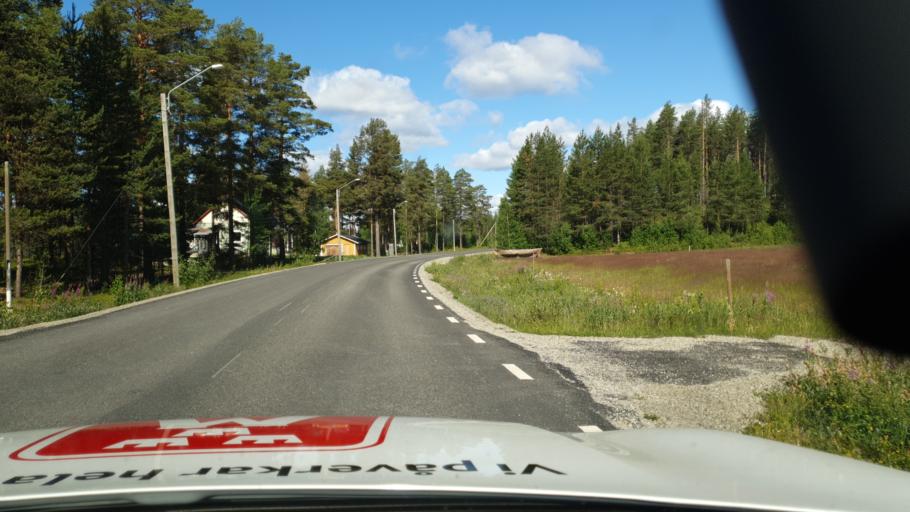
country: SE
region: Vaesterbotten
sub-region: Lycksele Kommun
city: Lycksele
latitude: 64.7649
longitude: 19.0476
